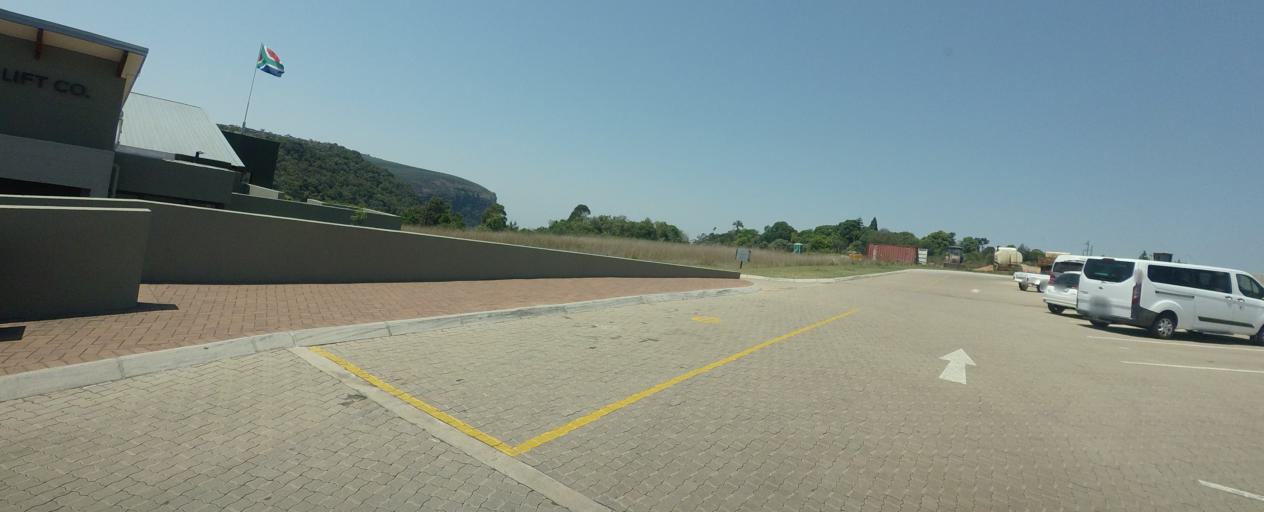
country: ZA
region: Mpumalanga
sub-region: Ehlanzeni District
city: Graksop
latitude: -24.9452
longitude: 30.8418
